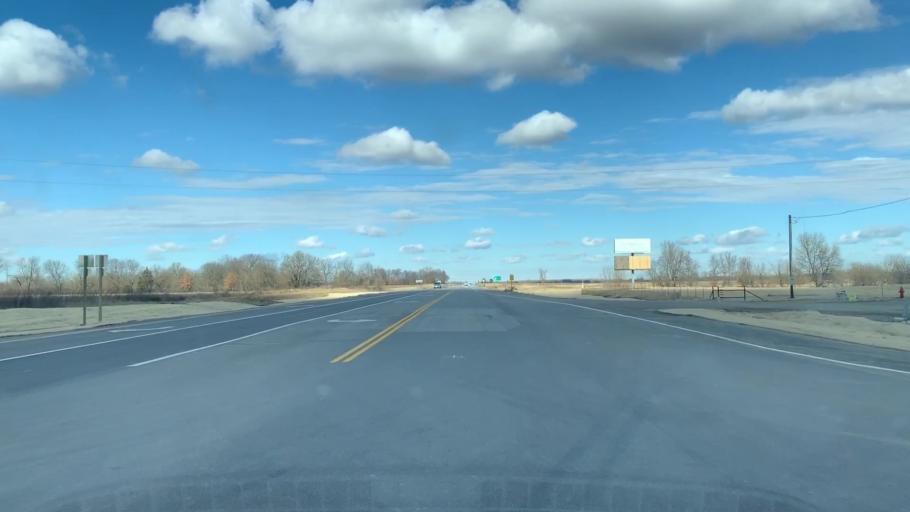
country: US
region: Kansas
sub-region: Cherokee County
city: Columbus
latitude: 37.2815
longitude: -94.8322
